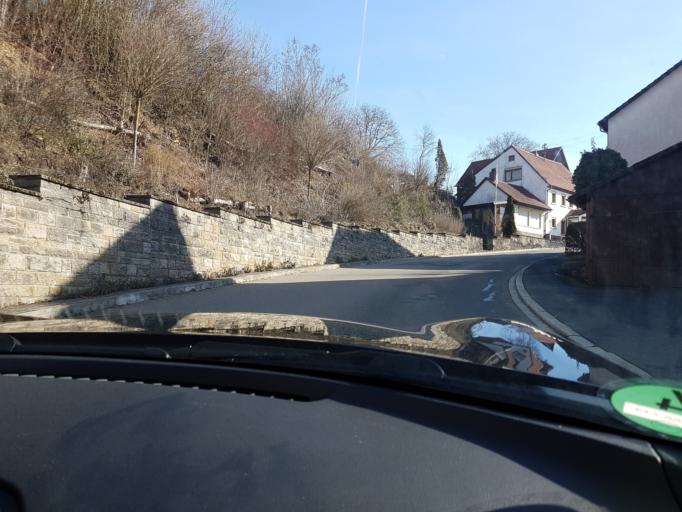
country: DE
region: Baden-Wuerttemberg
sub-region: Karlsruhe Region
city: Rosenberg
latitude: 49.4123
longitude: 9.5214
